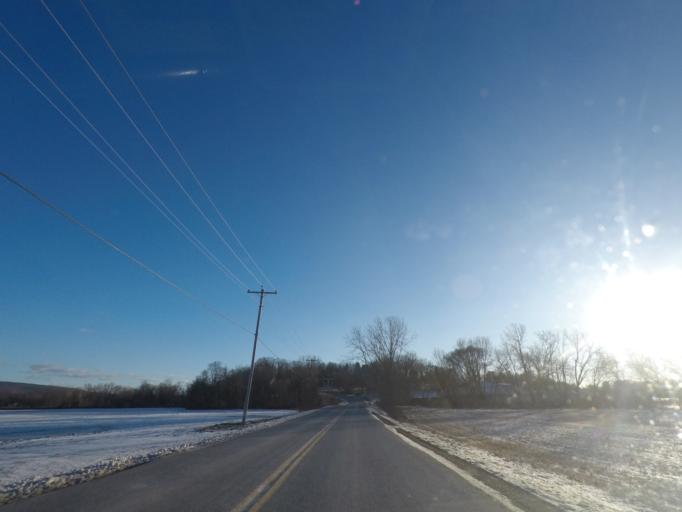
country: US
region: New York
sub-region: Rensselaer County
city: Poestenkill
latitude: 42.7031
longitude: -73.5814
